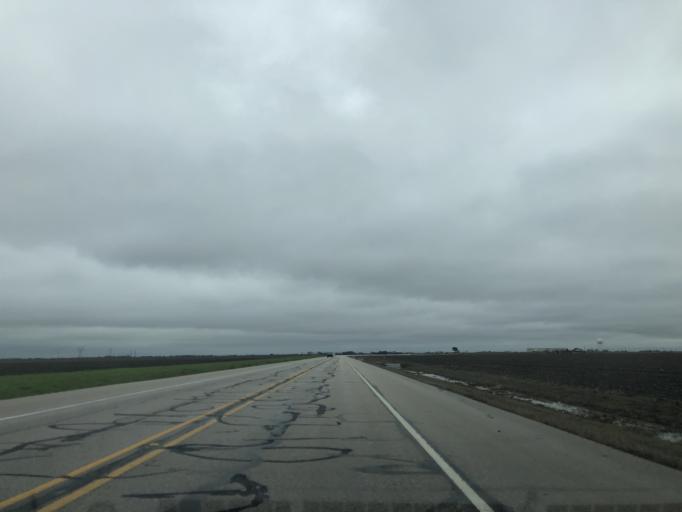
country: US
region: Texas
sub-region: Williamson County
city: Hutto
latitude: 30.6006
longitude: -97.5270
